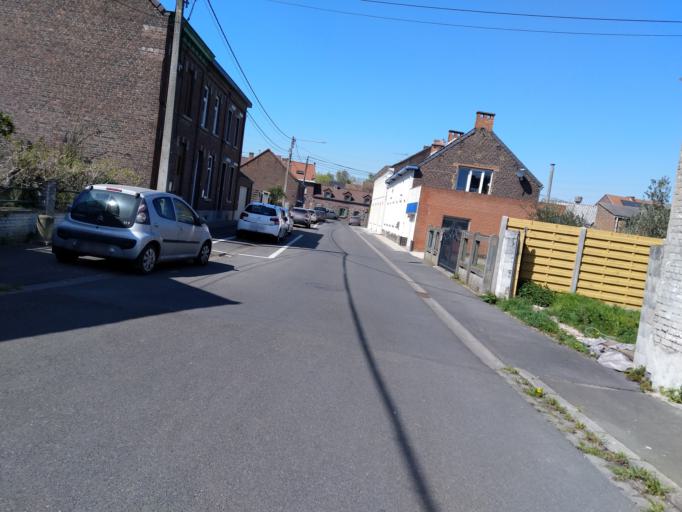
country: BE
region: Wallonia
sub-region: Province du Hainaut
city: Mons
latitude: 50.4754
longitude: 4.0091
